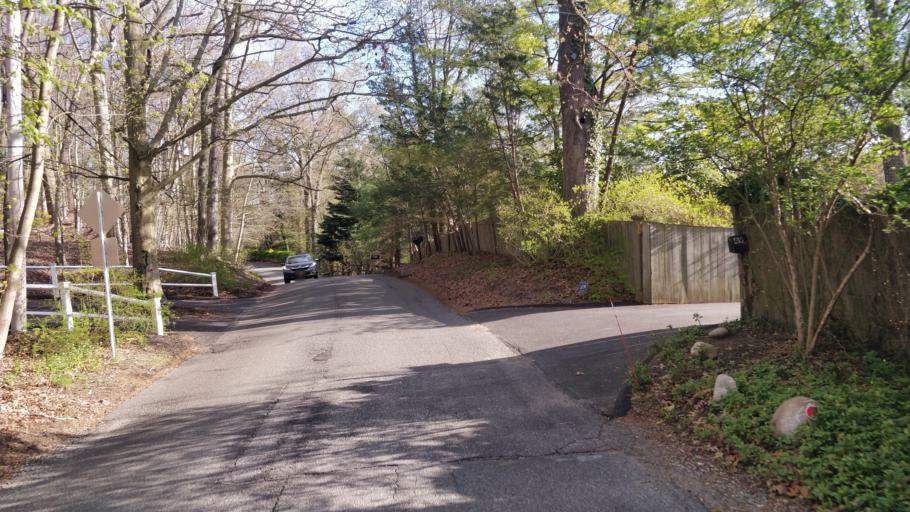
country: US
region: New York
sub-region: Suffolk County
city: Head of the Harbor
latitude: 40.8977
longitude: -73.1678
